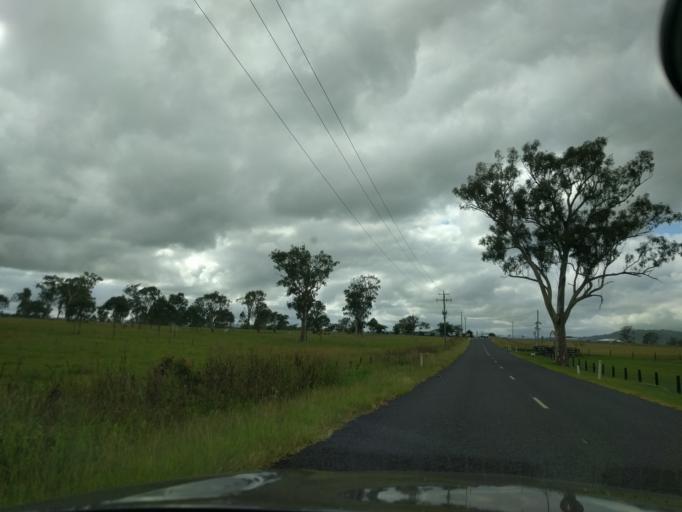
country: AU
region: Queensland
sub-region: Logan
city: Cedar Vale
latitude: -28.0058
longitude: 152.9916
